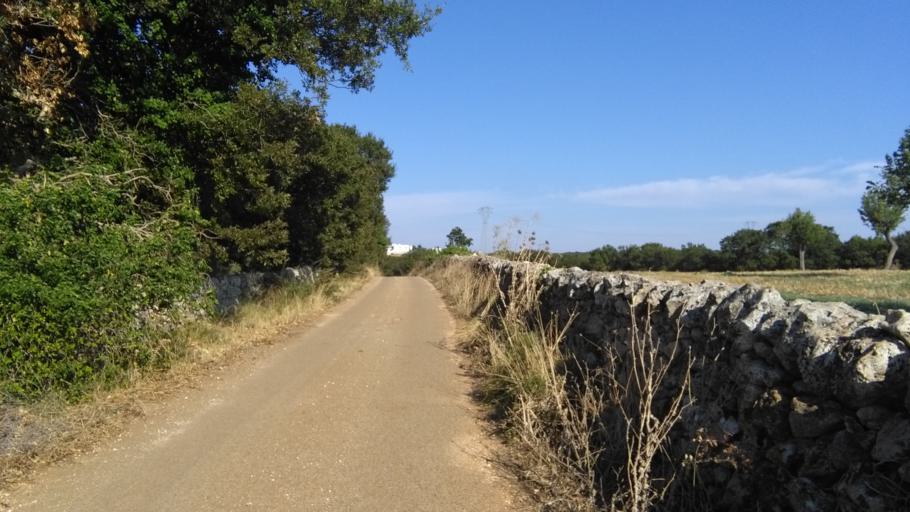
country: IT
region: Apulia
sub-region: Provincia di Bari
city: Putignano
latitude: 40.8199
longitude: 17.0440
